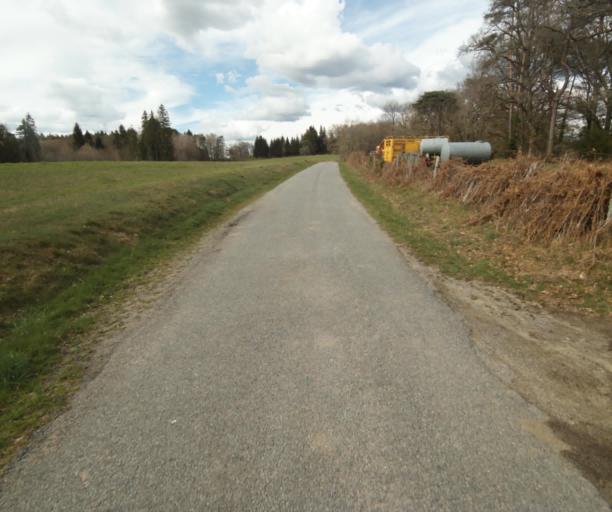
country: FR
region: Limousin
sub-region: Departement de la Correze
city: Argentat
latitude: 45.1953
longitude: 1.9272
